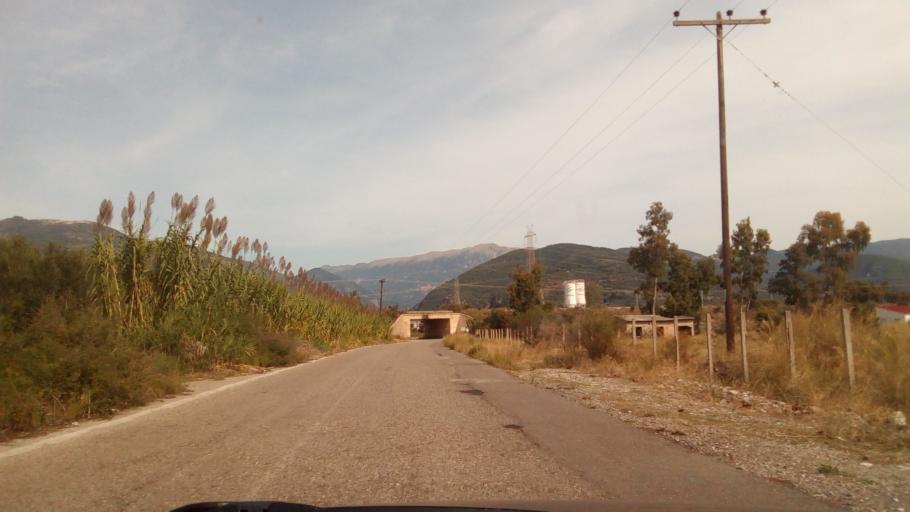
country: GR
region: West Greece
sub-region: Nomos Aitolias kai Akarnanias
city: Nafpaktos
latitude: 38.4064
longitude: 21.8800
